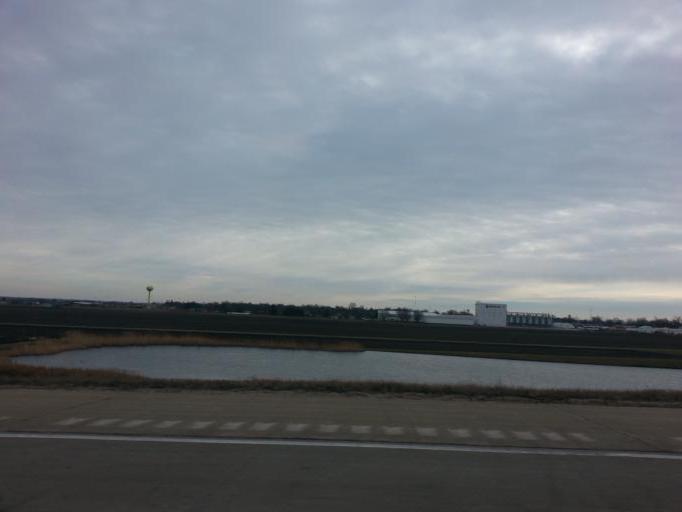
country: US
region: Illinois
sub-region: Woodford County
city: El Paso
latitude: 40.7400
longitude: -89.0344
